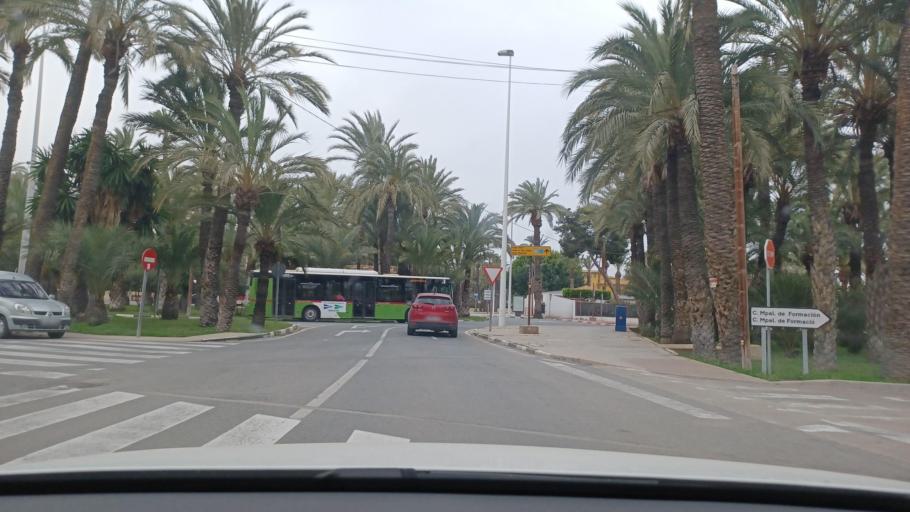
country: ES
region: Valencia
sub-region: Provincia de Alicante
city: Elche
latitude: 38.2569
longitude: -0.6924
